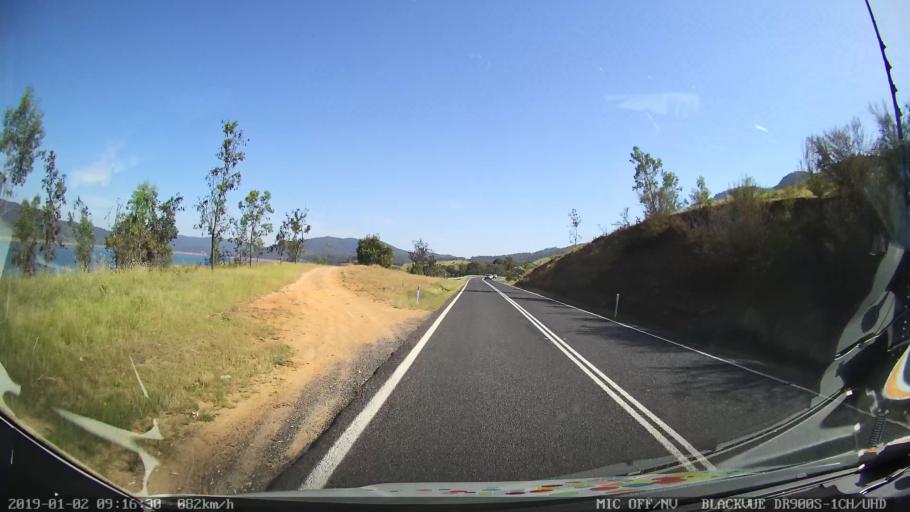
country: AU
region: New South Wales
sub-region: Tumut Shire
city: Tumut
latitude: -35.4525
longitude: 148.2843
